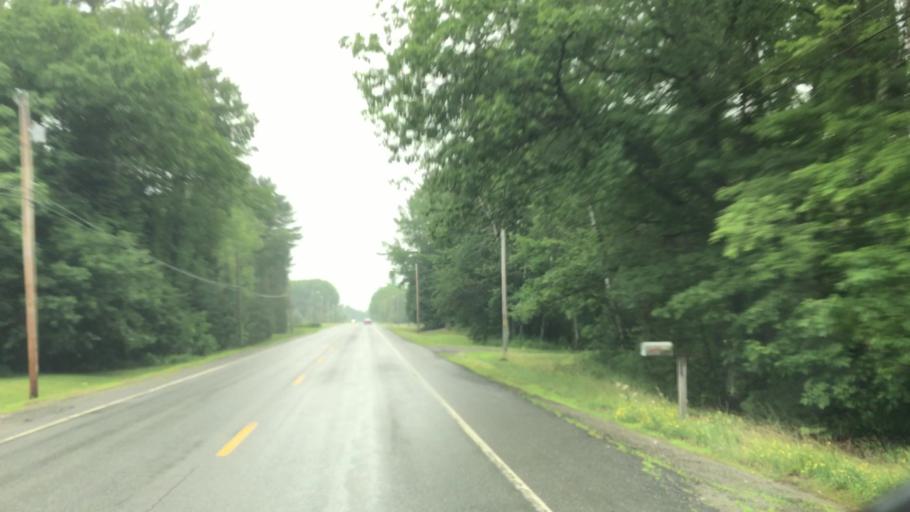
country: US
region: Maine
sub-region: Penobscot County
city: Howland
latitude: 45.2595
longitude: -68.6379
